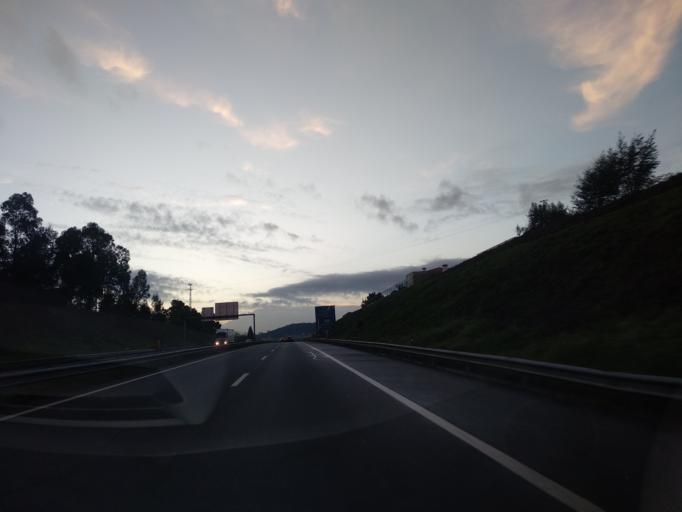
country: PT
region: Braga
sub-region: Vila Nova de Famalicao
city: Vila Nova de Famalicao
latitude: 41.3834
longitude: -8.5069
